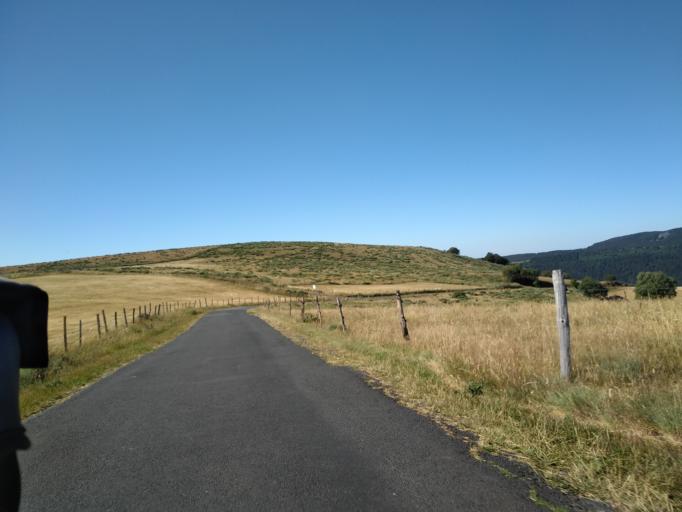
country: FR
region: Auvergne
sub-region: Departement du Cantal
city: Pierrefort
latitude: 45.0127
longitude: 2.8172
